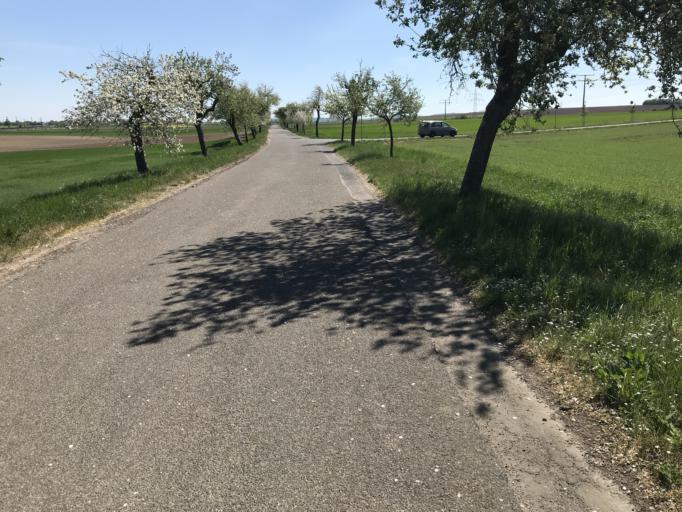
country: DE
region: Bavaria
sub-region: Regierungsbezirk Unterfranken
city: Iphofen
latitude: 49.6915
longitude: 10.2630
